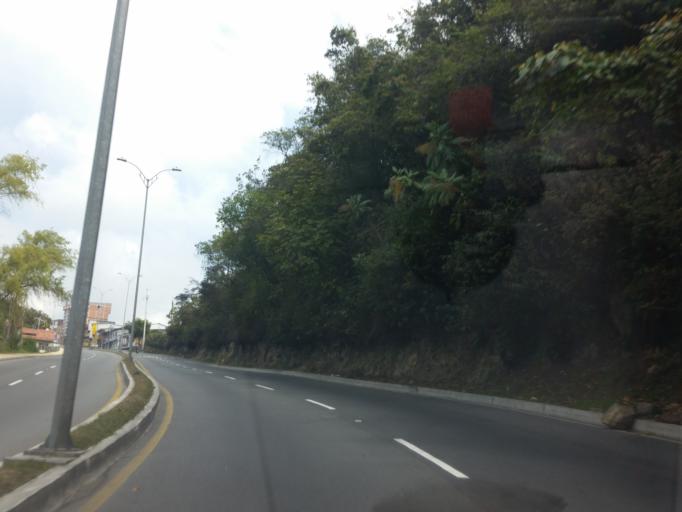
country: CO
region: Caldas
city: Manizales
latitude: 5.0588
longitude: -75.5273
